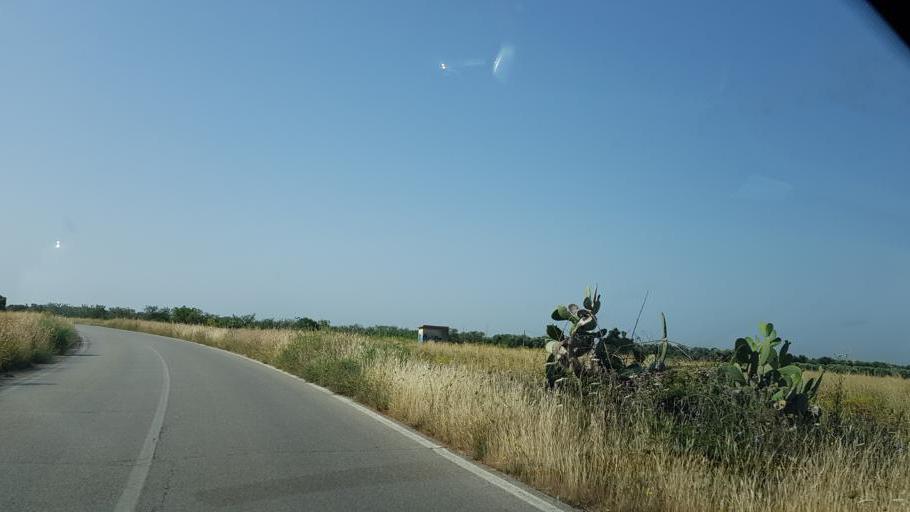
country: IT
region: Apulia
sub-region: Provincia di Brindisi
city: Mesagne
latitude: 40.5224
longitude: 17.8214
